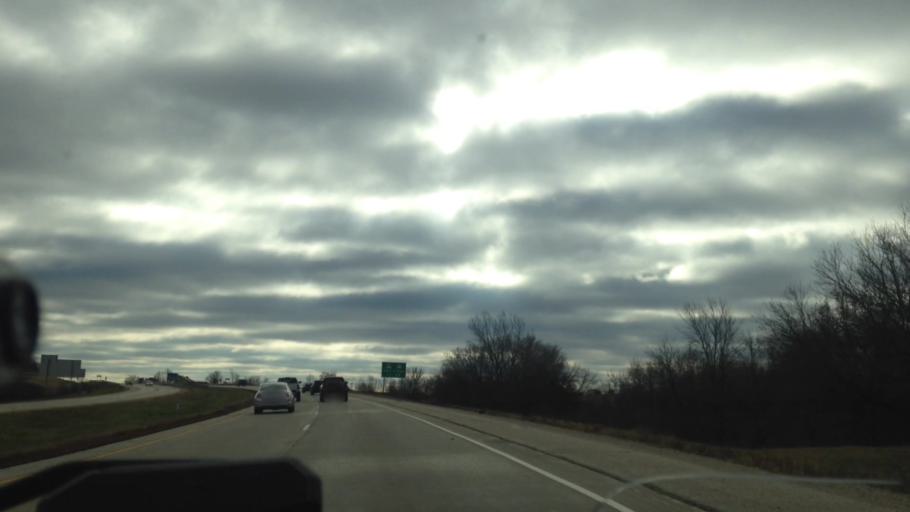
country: US
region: Wisconsin
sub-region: Washington County
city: West Bend
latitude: 43.4102
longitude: -88.2045
